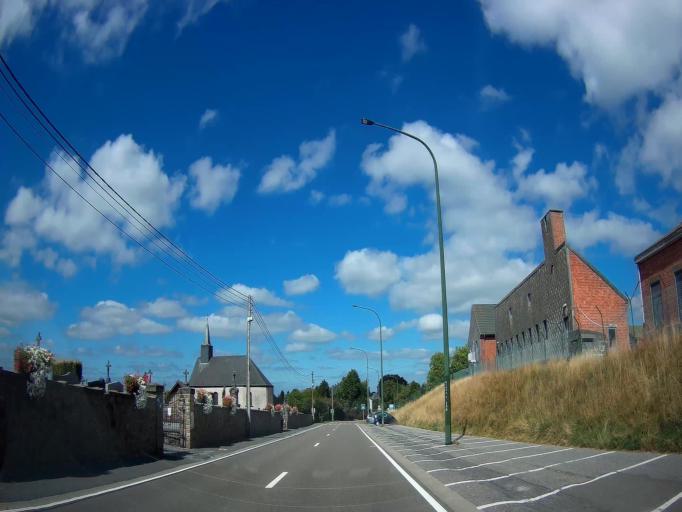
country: BE
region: Wallonia
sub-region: Province du Luxembourg
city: Bastogne
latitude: 50.0086
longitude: 5.7180
